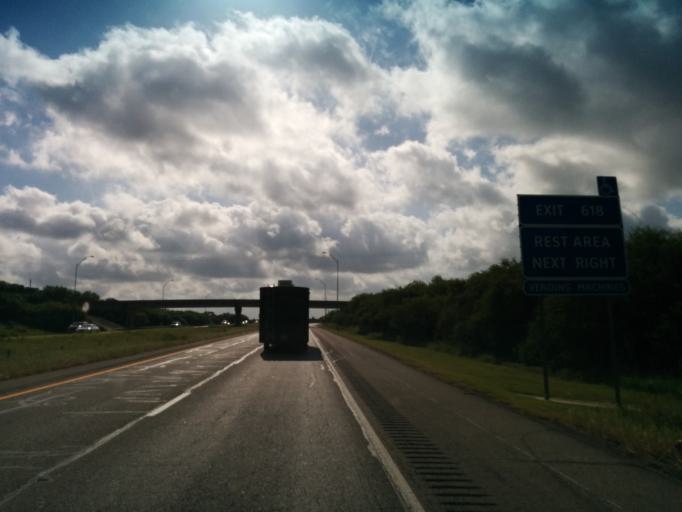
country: US
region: Texas
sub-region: Guadalupe County
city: Seguin
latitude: 29.6148
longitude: -97.8132
